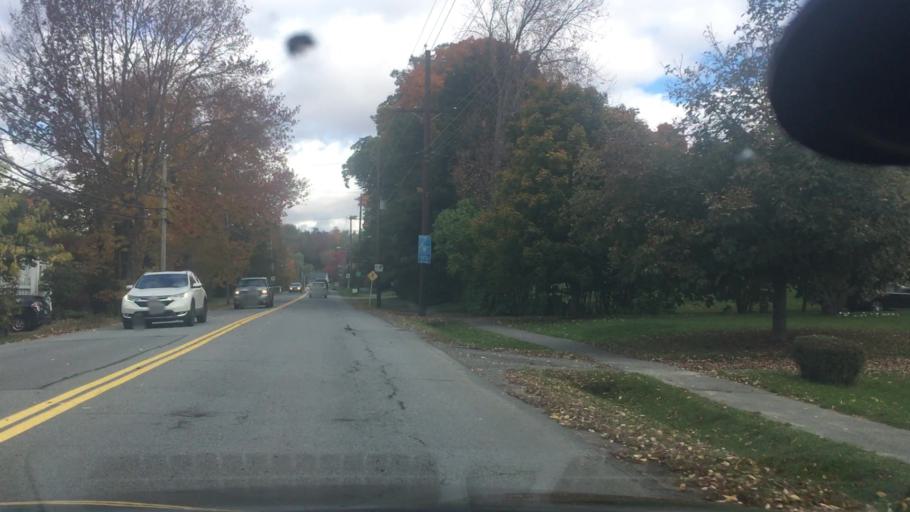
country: CA
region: Nova Scotia
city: Windsor
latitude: 44.9826
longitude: -64.1304
